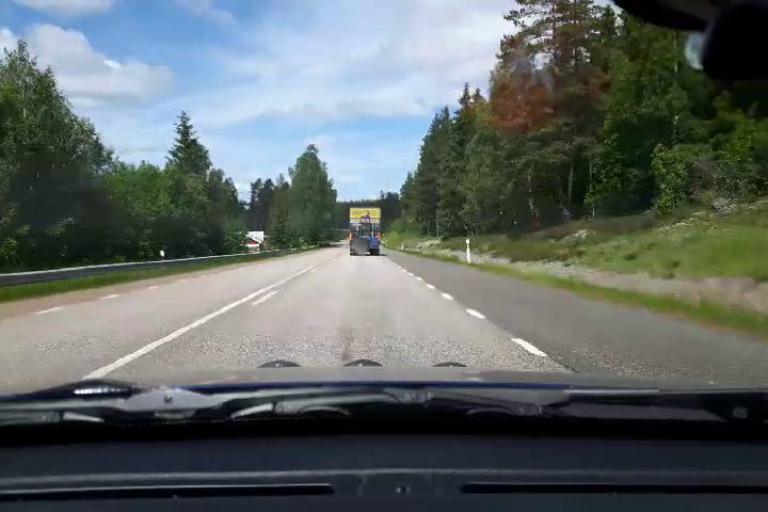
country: SE
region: Uppsala
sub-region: Osthammars Kommun
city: Bjorklinge
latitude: 60.0950
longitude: 17.5541
